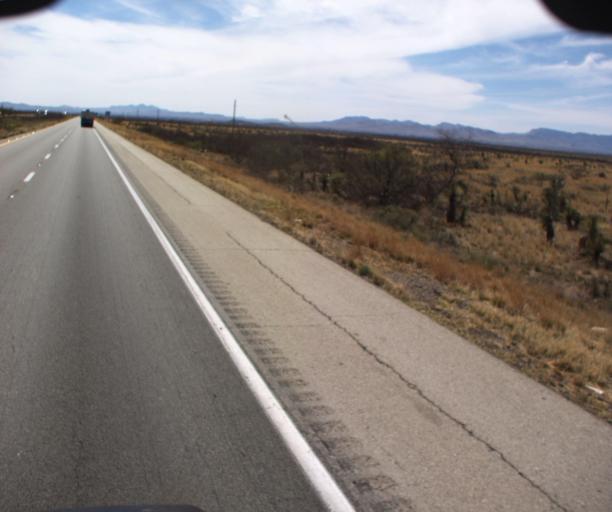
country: US
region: Arizona
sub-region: Cochise County
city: Willcox
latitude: 32.3298
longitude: -109.7694
